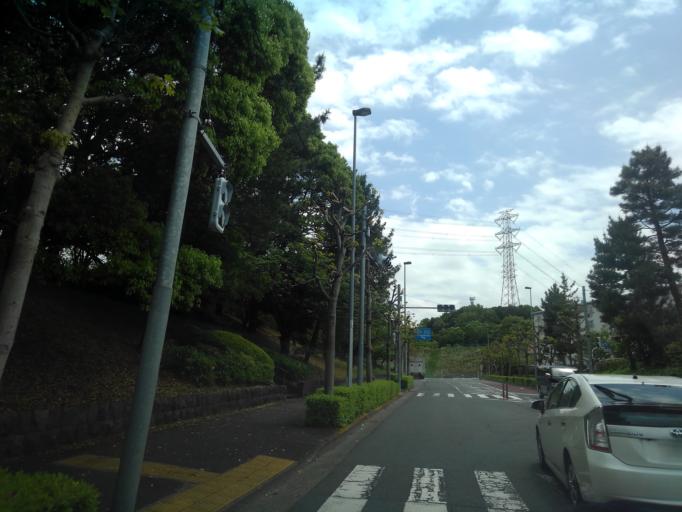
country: JP
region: Tokyo
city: Hino
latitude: 35.6199
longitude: 139.4524
